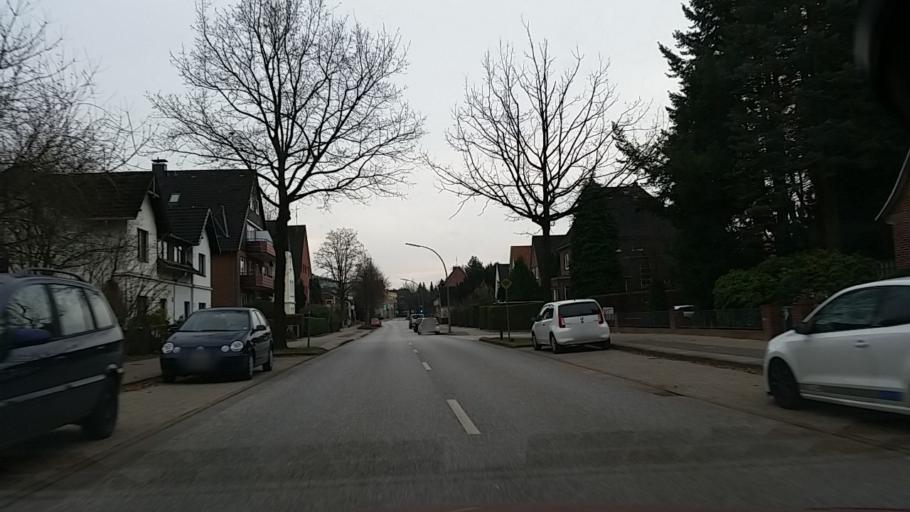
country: DE
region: Hamburg
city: Stellingen
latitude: 53.6258
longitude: 9.9510
